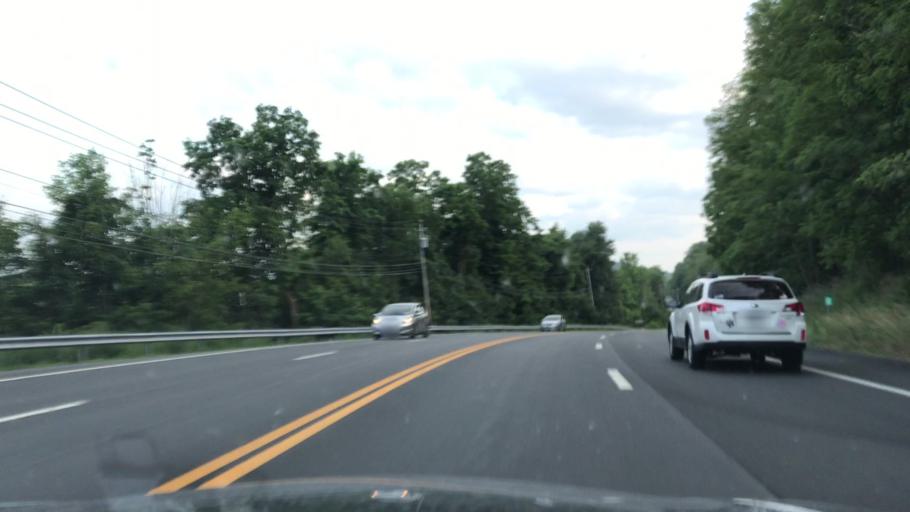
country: US
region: New York
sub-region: Orange County
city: Harriman
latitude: 41.2385
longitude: -74.1770
